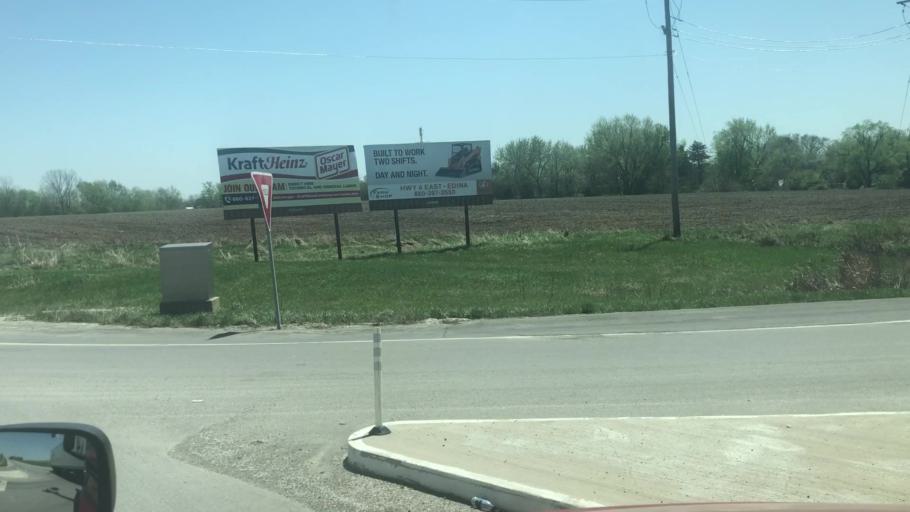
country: US
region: Missouri
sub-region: Adair County
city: Kirksville
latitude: 40.2162
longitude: -92.5922
